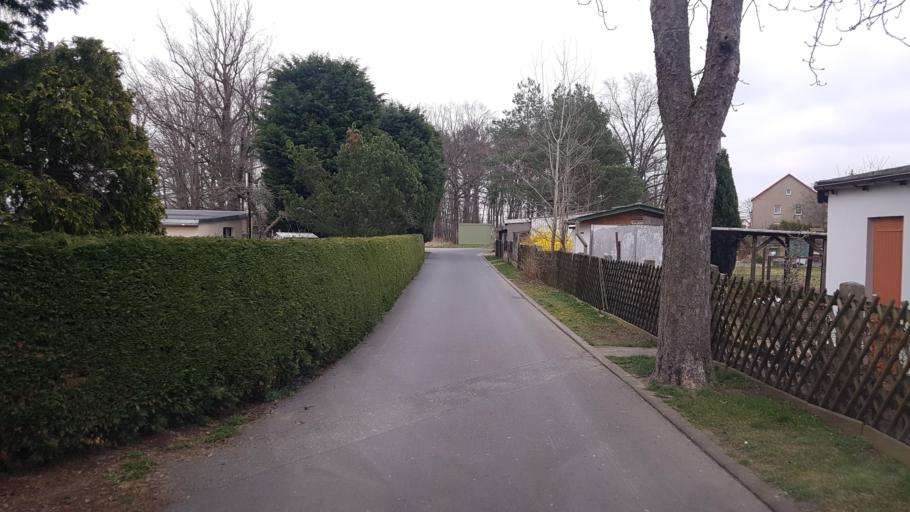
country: DE
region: Saxony
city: Nauwalde
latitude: 51.4224
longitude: 13.4496
